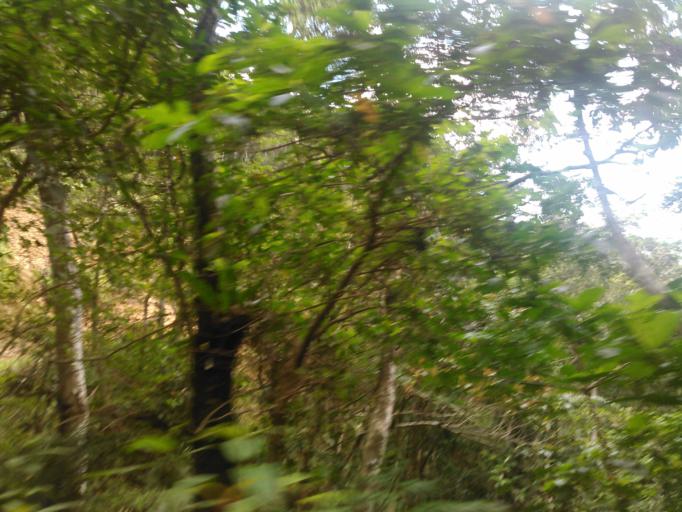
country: TW
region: Taiwan
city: Hengchun
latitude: 22.2672
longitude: 120.8208
